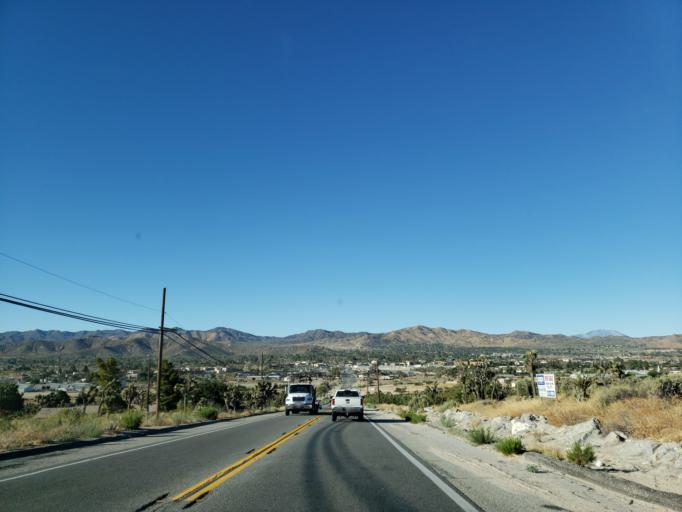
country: US
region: California
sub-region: San Bernardino County
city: Yucca Valley
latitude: 34.1335
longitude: -116.4128
